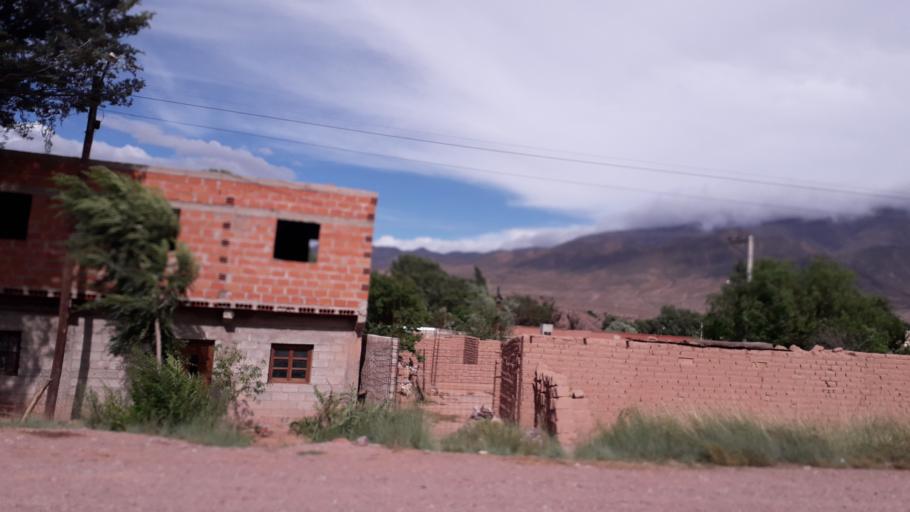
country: AR
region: Jujuy
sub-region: Departamento de Humahuaca
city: Humahuaca
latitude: -23.3058
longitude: -65.3547
